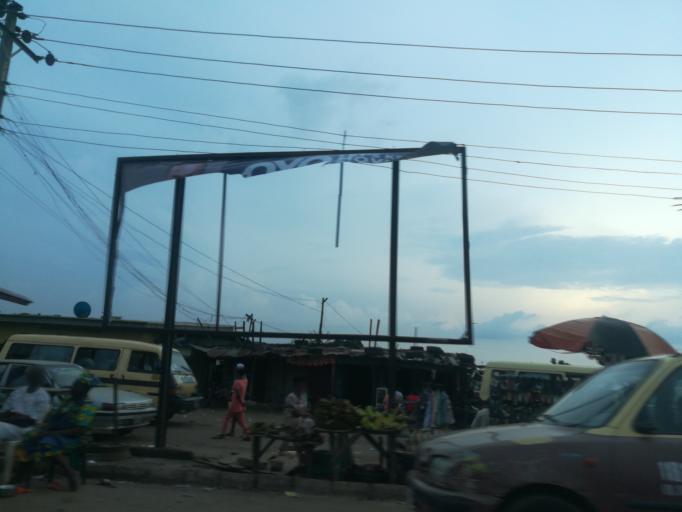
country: NG
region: Oyo
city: Ibadan
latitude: 7.4232
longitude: 3.8987
